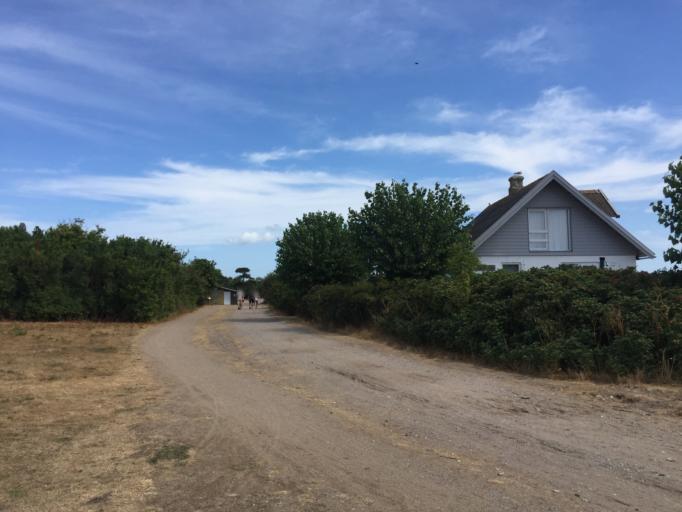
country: DK
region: Central Jutland
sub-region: Samso Kommune
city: Tranebjerg
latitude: 55.9504
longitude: 10.4527
